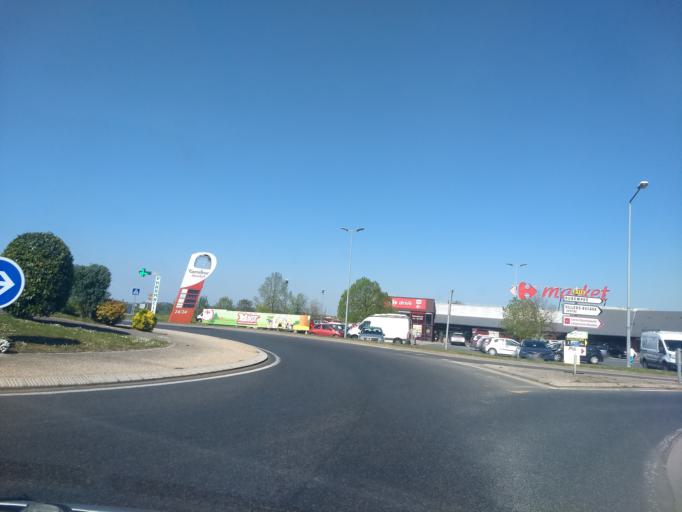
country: FR
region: Picardie
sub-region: Departement de la Somme
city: Villers-Bocage
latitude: 50.0037
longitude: 2.3126
